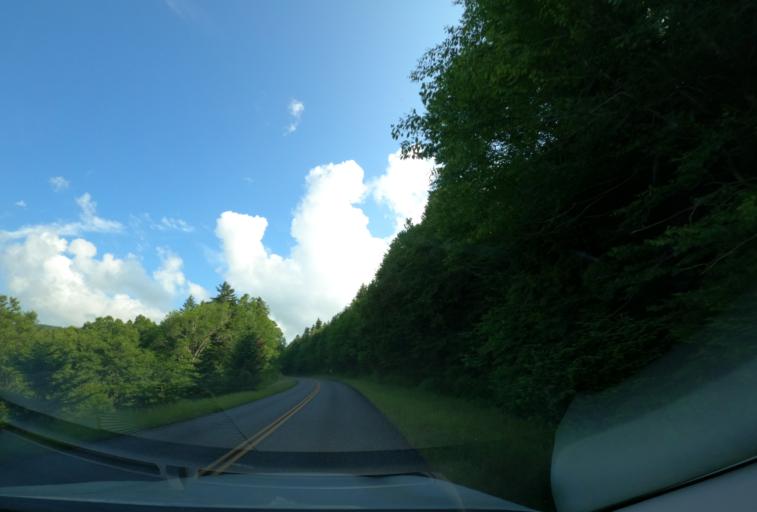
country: US
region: North Carolina
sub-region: Haywood County
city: Hazelwood
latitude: 35.3331
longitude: -82.9658
